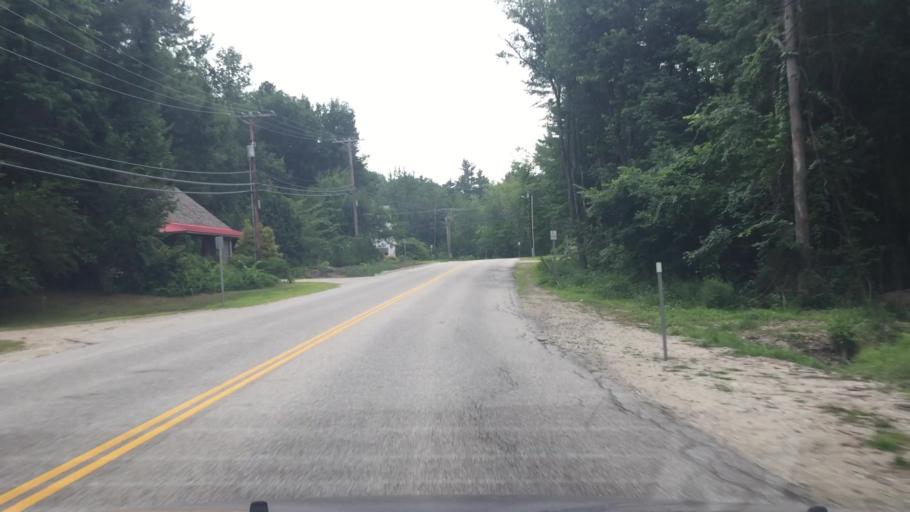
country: US
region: New Hampshire
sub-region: Carroll County
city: North Conway
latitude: 44.0559
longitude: -71.1352
